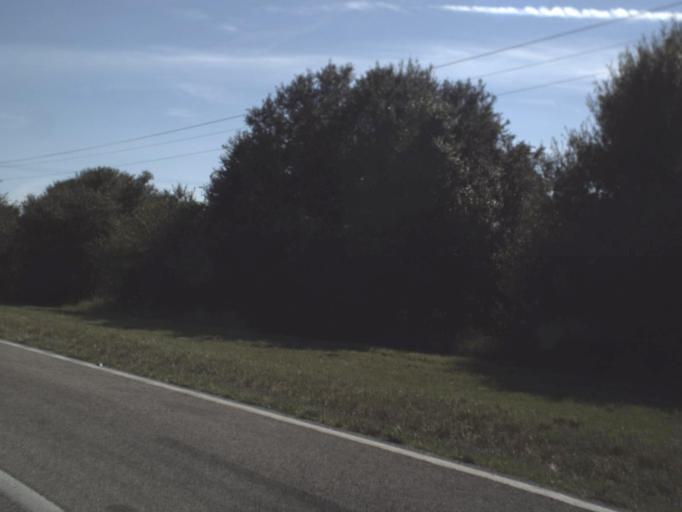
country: US
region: Florida
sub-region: Highlands County
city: Placid Lakes
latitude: 27.0280
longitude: -81.3417
